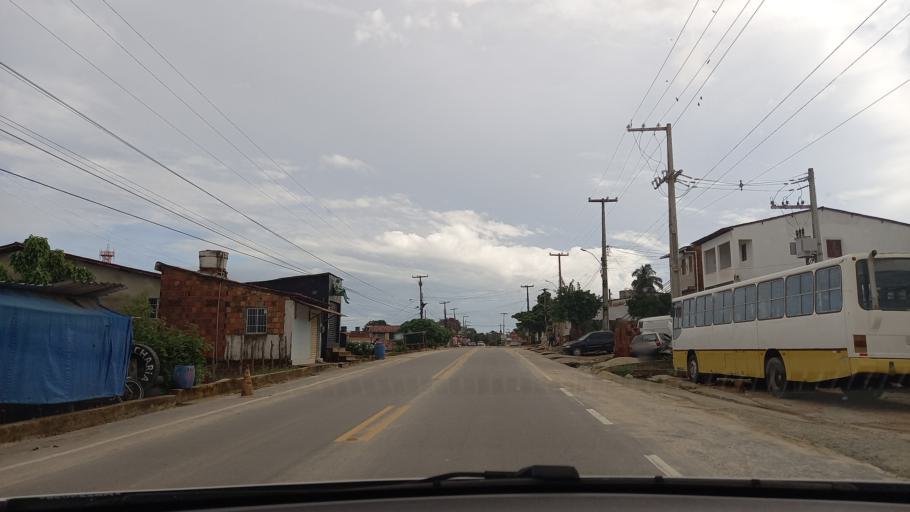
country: BR
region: Alagoas
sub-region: Maragogi
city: Maragogi
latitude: -8.9827
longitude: -35.1958
